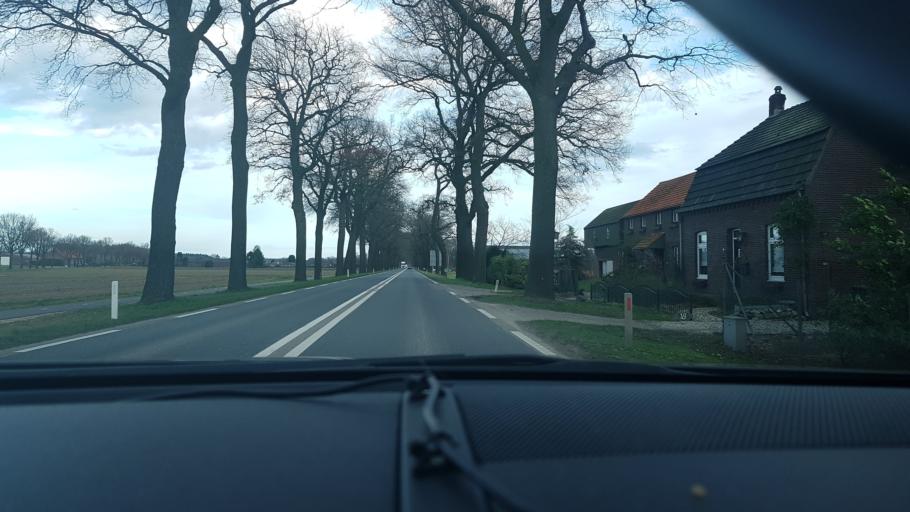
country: NL
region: Limburg
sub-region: Gemeente Beesel
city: Beesel
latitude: 51.2837
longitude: 6.0247
